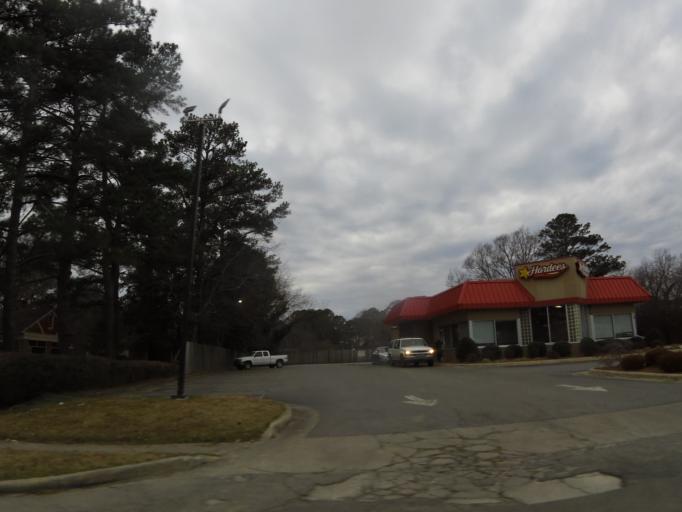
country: US
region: North Carolina
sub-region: Halifax County
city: Scotland Neck
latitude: 36.1252
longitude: -77.4252
